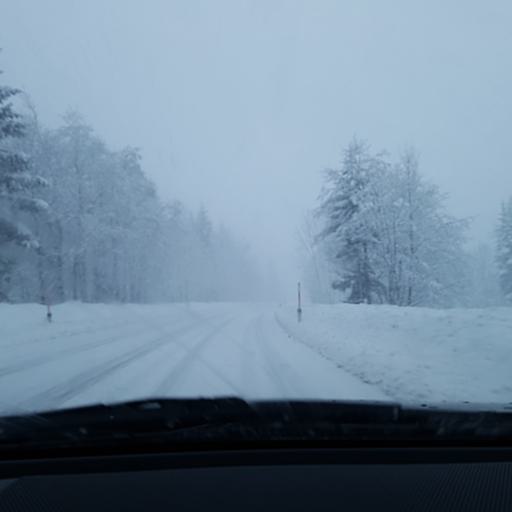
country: AT
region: Salzburg
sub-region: Politischer Bezirk Salzburg-Umgebung
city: Strobl
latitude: 47.5903
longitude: 13.4957
